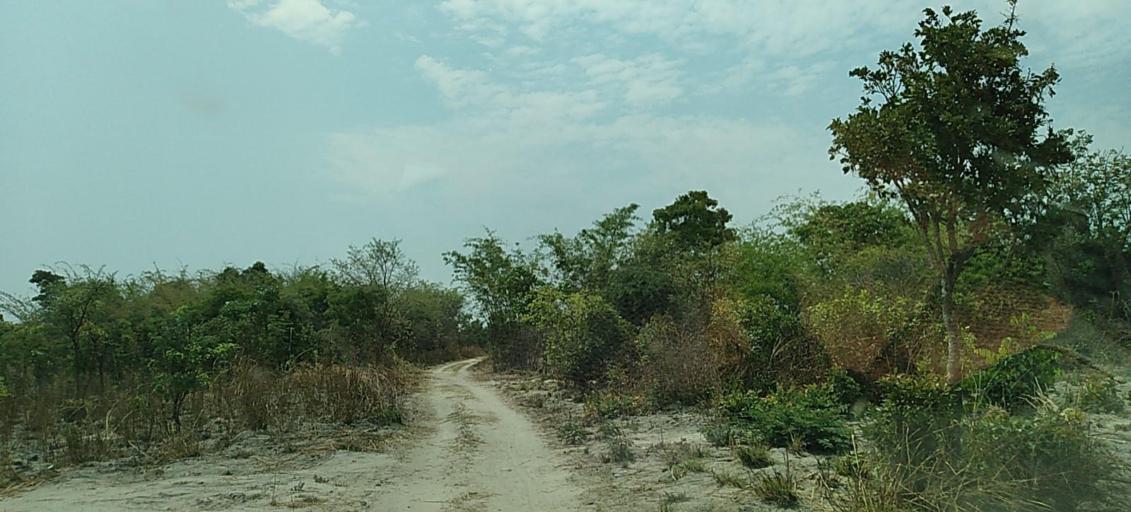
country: ZM
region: Copperbelt
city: Kalulushi
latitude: -12.9430
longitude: 28.1220
